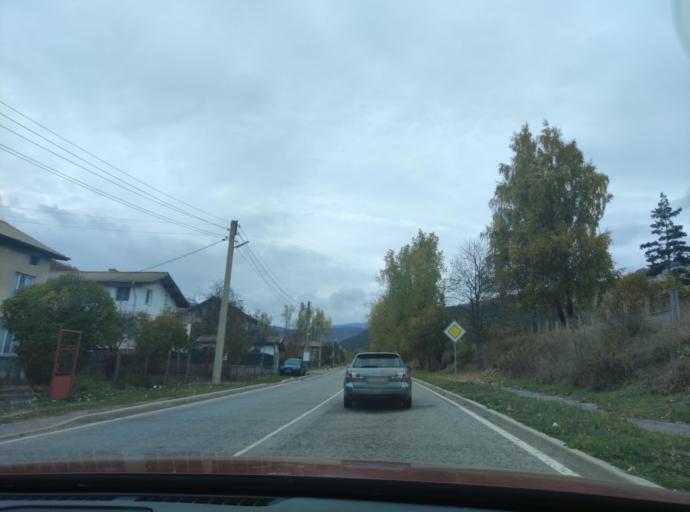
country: BG
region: Sofiya
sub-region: Obshtina Godech
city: Godech
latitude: 43.0786
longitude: 23.1072
